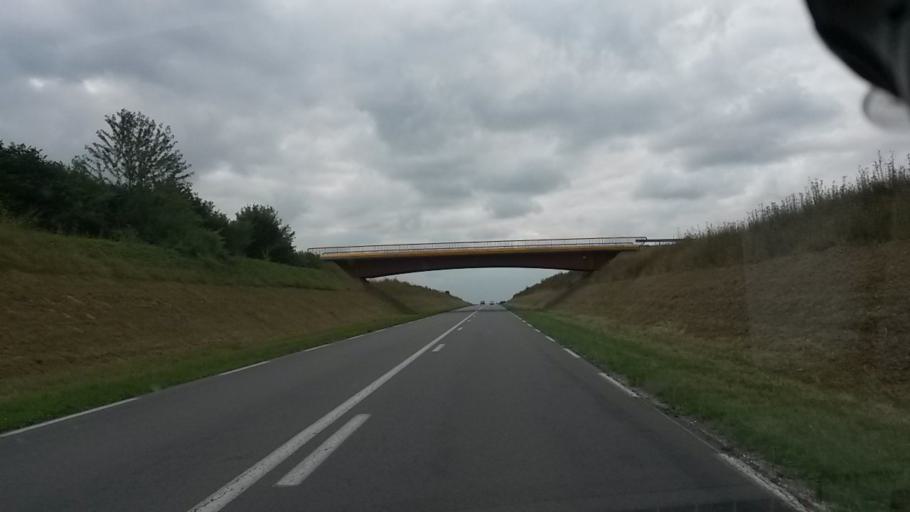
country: FR
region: Picardie
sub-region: Departement de la Somme
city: Corbie
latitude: 49.9572
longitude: 2.4777
